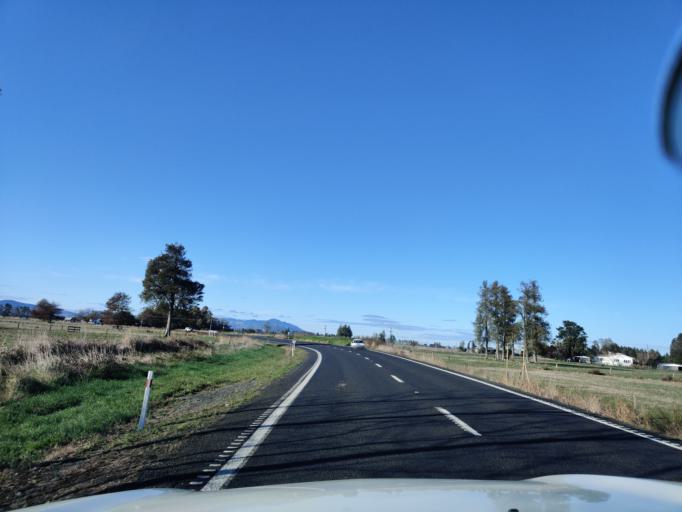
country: NZ
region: Waikato
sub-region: Hauraki District
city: Ngatea
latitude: -37.3089
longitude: 175.5644
